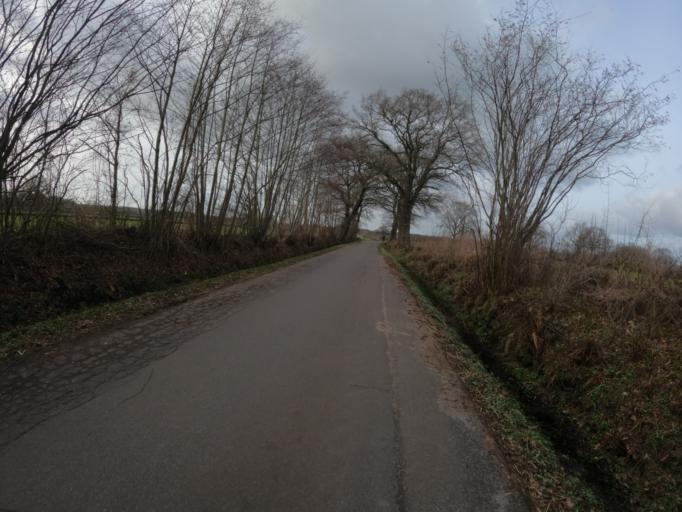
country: DE
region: Schleswig-Holstein
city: Rellingen
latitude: 53.5921
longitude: 9.7955
